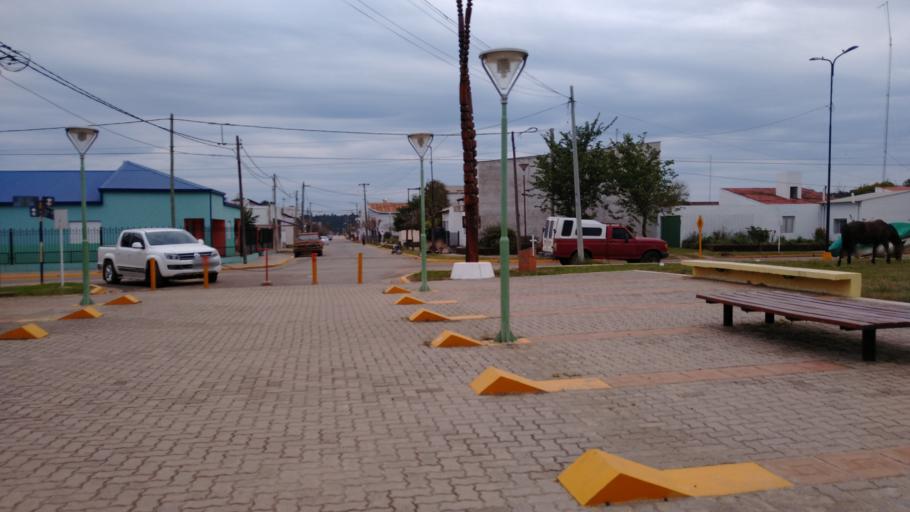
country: AR
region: Entre Rios
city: Villa del Rosario
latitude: -30.7962
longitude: -57.9148
